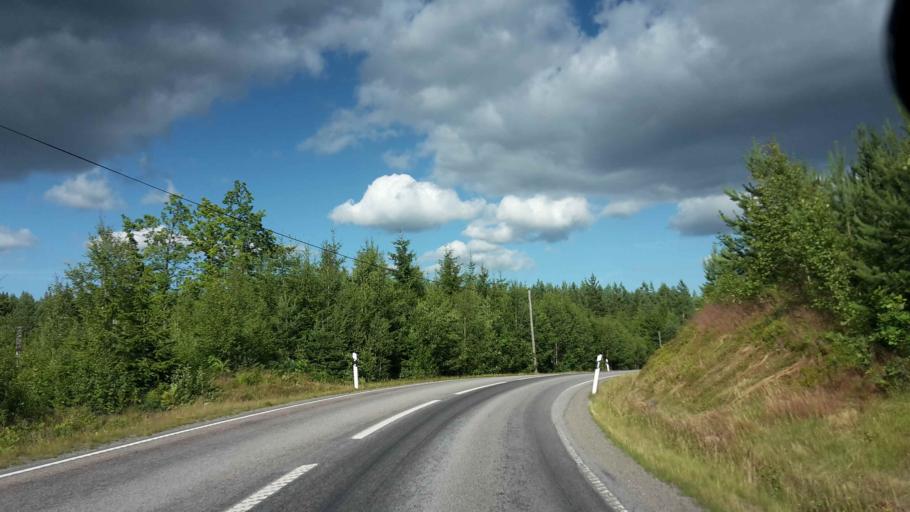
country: SE
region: OEstergoetland
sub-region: Motala Kommun
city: Borensberg
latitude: 58.8018
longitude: 15.4393
